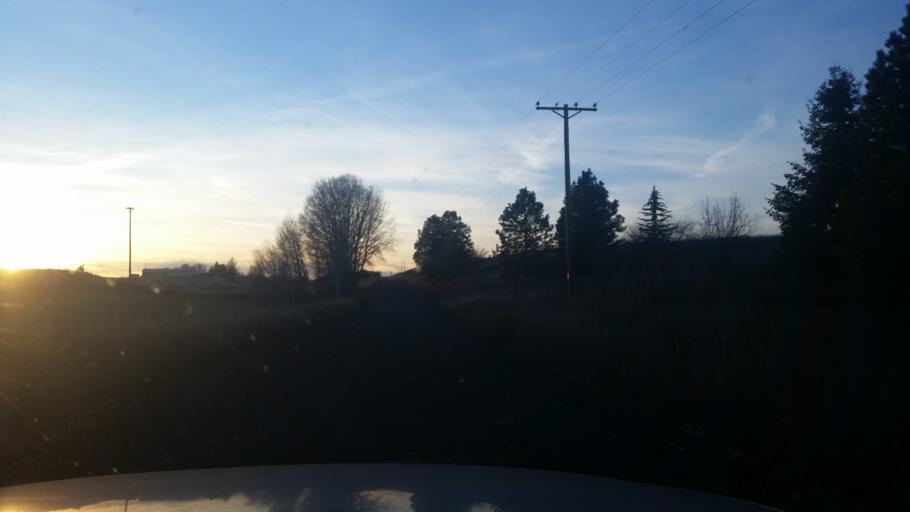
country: US
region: Washington
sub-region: Spokane County
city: Veradale
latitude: 47.5077
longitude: -117.1224
